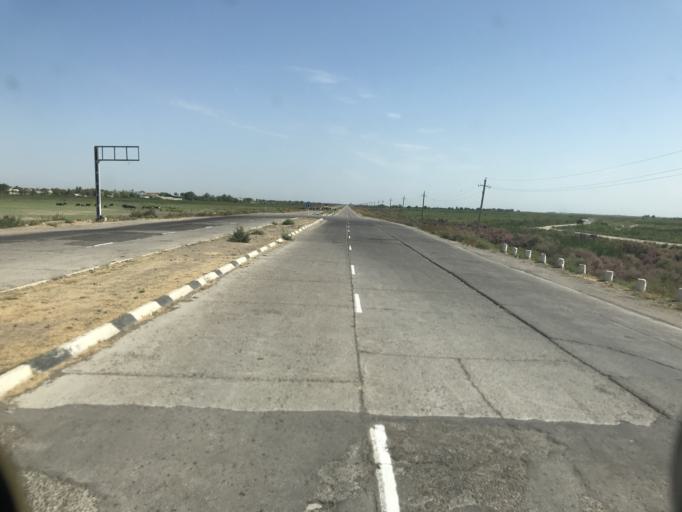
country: KZ
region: Ongtustik Qazaqstan
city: Myrzakent
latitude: 40.7492
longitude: 68.5379
